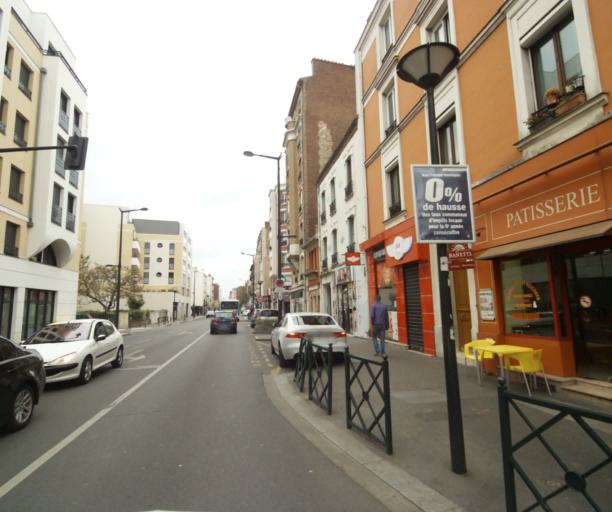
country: FR
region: Ile-de-France
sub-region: Departement des Hauts-de-Seine
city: Asnieres-sur-Seine
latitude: 48.9194
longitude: 2.2803
